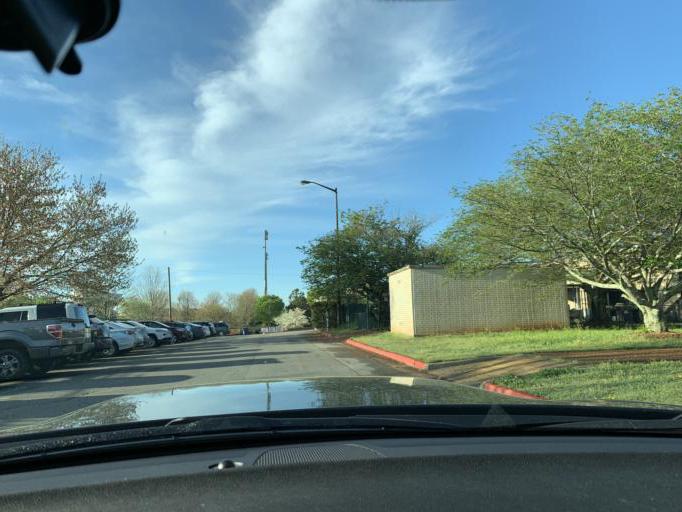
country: US
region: Georgia
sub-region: Fulton County
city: Roswell
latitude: 34.0641
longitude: -84.3806
